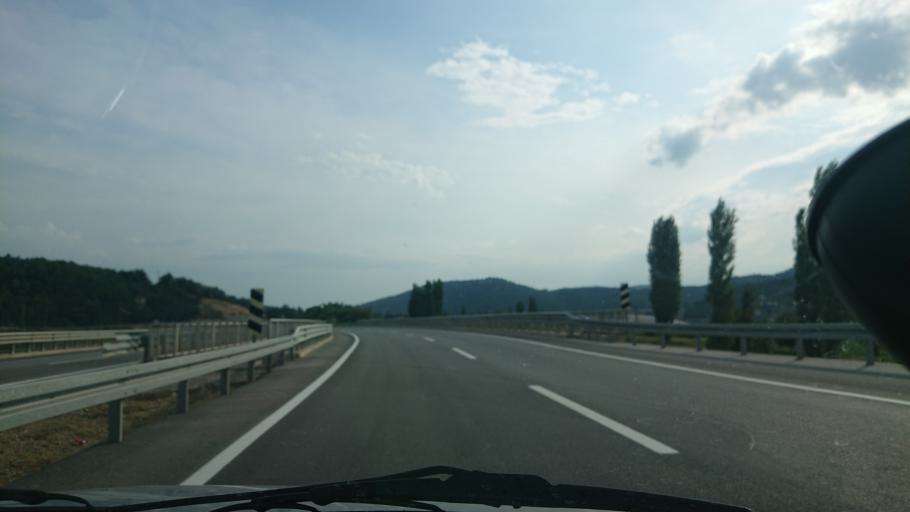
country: TR
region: Kuetahya
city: Gediz
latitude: 38.9299
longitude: 29.3054
